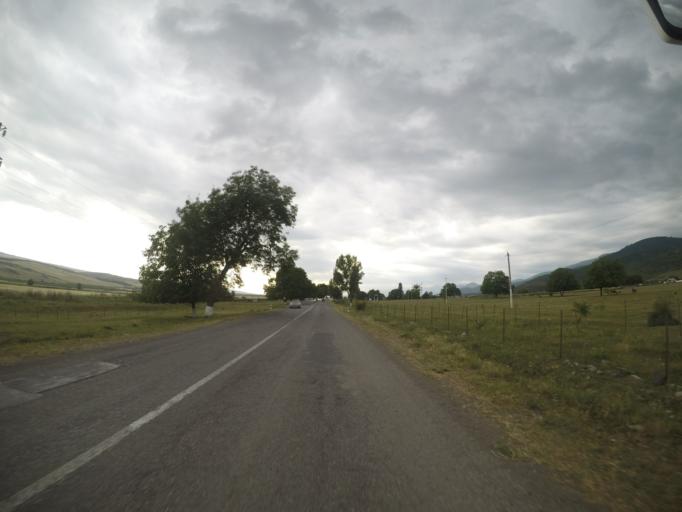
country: AZ
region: Ismayilli
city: Ismayilli
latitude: 40.7593
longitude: 48.2161
